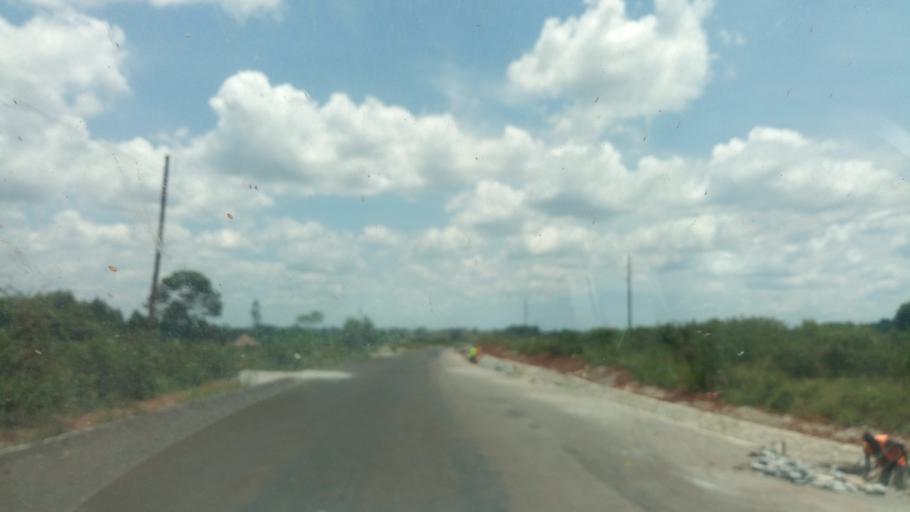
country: UG
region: Western Region
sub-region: Kiryandongo District
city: Kiryandongo
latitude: 1.7900
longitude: 31.9484
